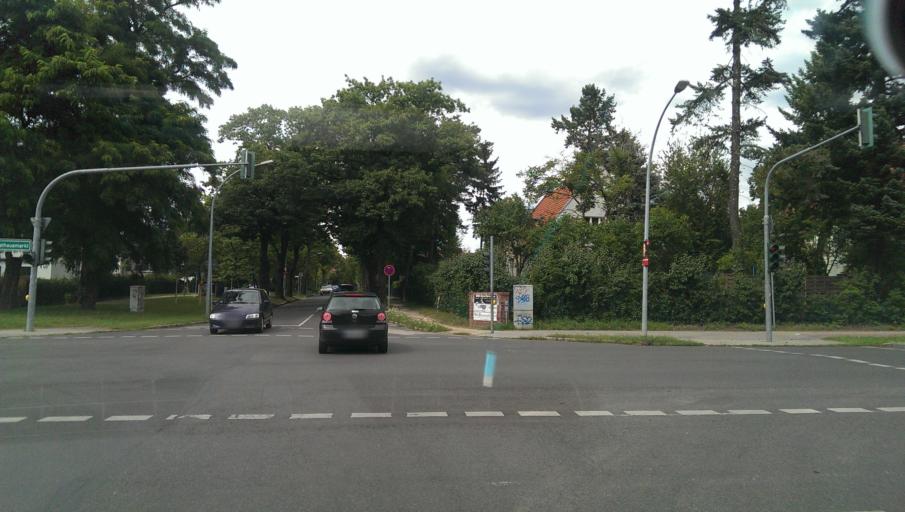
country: DE
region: Brandenburg
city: Kleinmachnow
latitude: 52.4049
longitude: 13.2255
